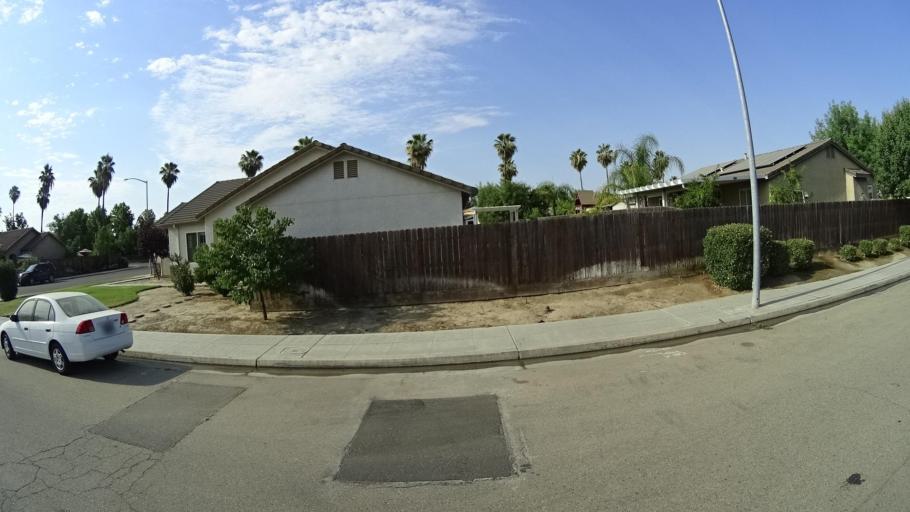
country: US
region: California
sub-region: Fresno County
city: Sunnyside
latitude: 36.7204
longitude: -119.7018
